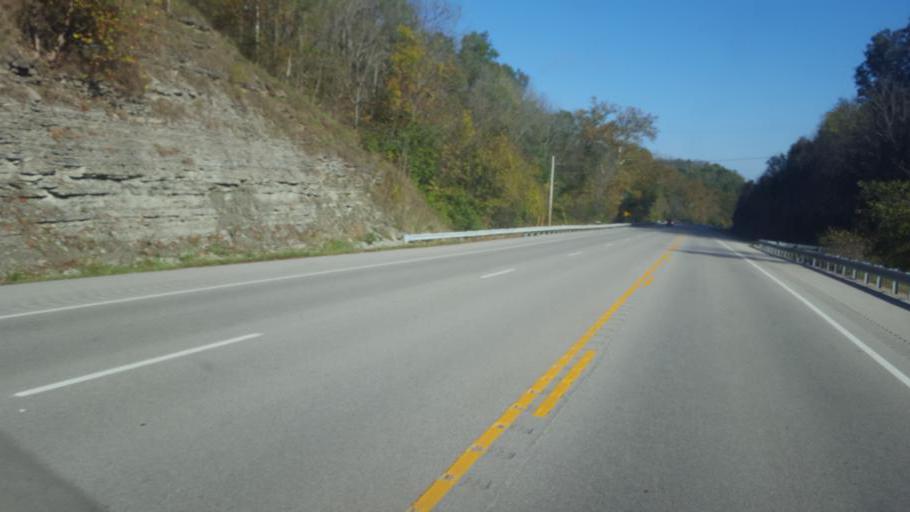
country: US
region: Kentucky
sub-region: Mason County
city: Maysville
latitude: 38.6104
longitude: -83.7564
